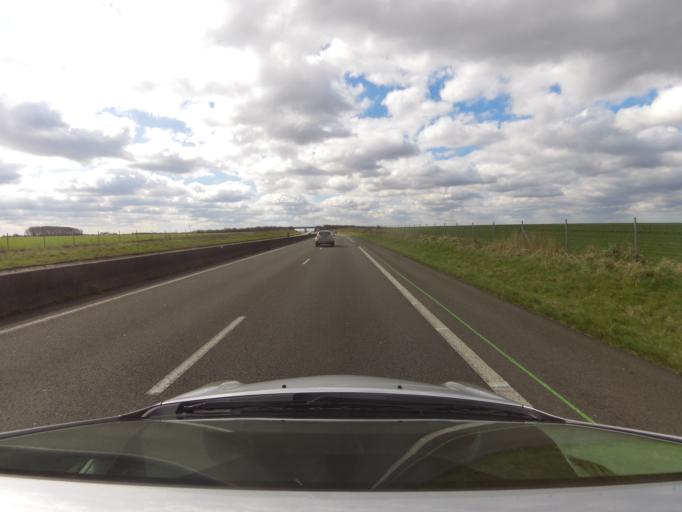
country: FR
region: Picardie
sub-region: Departement de la Somme
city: Sailly-Flibeaucourt
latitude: 50.1844
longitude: 1.7540
